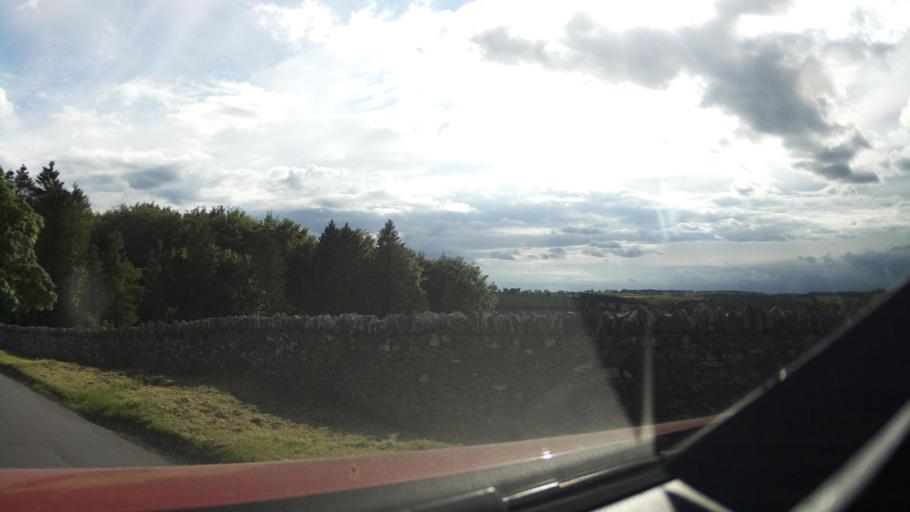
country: GB
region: England
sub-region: Gloucestershire
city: Westfield
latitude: 51.9202
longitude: -1.8469
